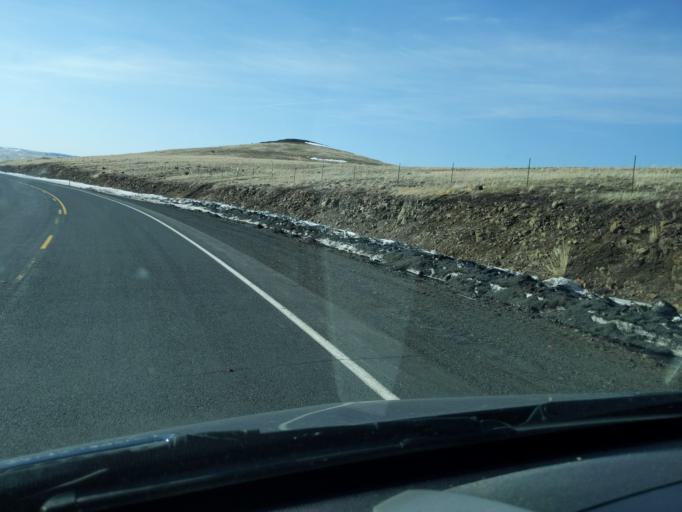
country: US
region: Oregon
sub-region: Umatilla County
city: Pilot Rock
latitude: 45.2999
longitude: -118.9884
